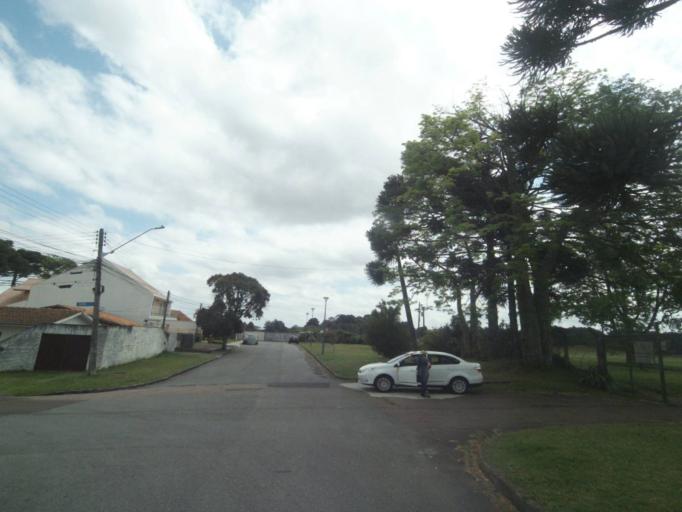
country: BR
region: Parana
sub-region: Curitiba
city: Curitiba
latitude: -25.4095
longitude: -49.2280
